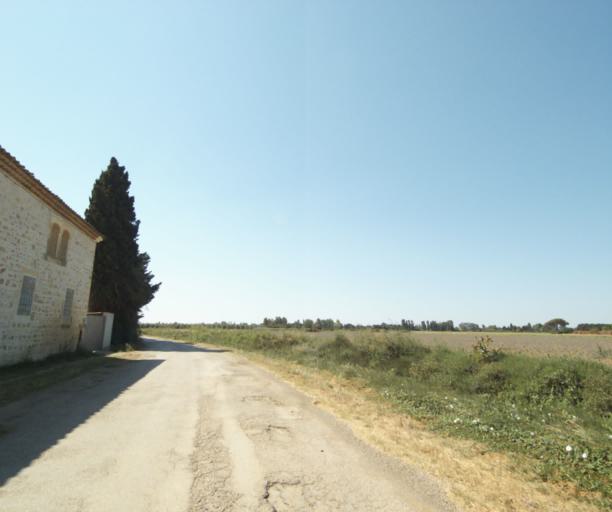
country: FR
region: Languedoc-Roussillon
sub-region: Departement de l'Herault
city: Marsillargues
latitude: 43.6481
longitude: 4.1670
